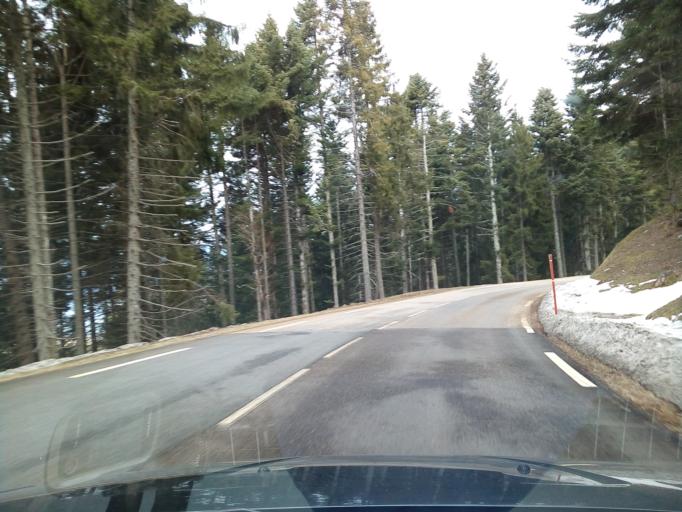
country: FR
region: Rhone-Alpes
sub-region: Departement de l'Isere
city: Revel
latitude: 45.1386
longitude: 5.8736
